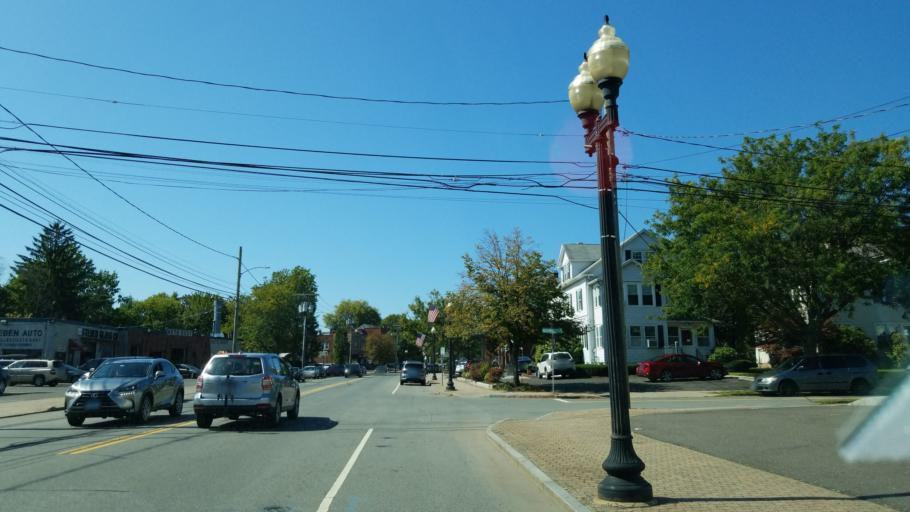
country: US
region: Connecticut
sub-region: Hartford County
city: West Hartford
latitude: 41.7566
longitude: -72.7272
